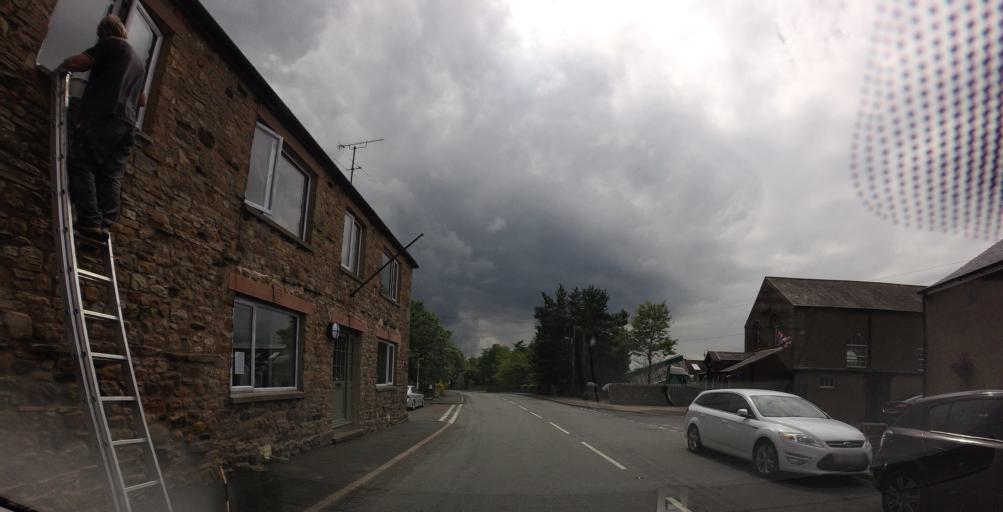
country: GB
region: England
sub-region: Cumbria
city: Kirkby Stephen
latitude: 54.5257
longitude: -2.3187
